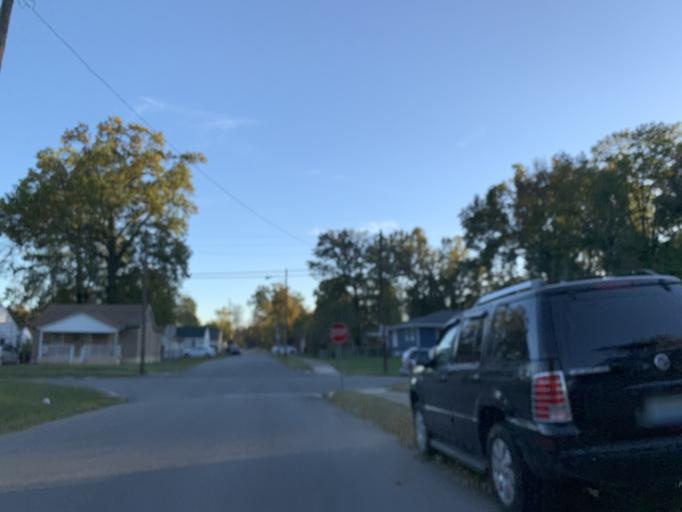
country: US
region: Indiana
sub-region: Floyd County
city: New Albany
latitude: 38.2433
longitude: -85.8279
